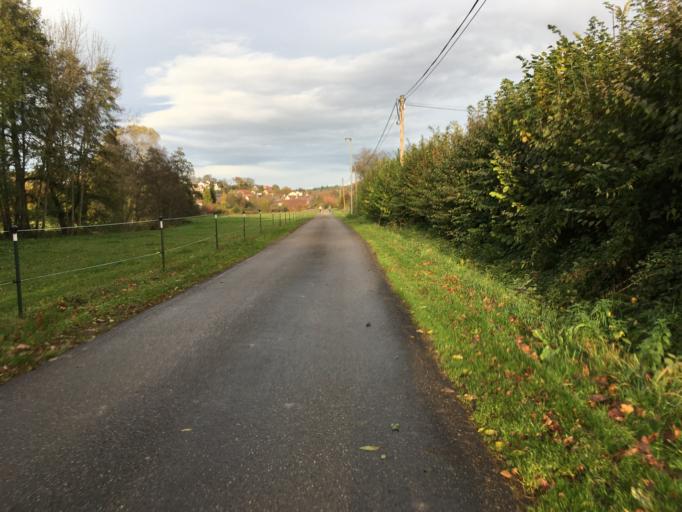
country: DE
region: Baden-Wuerttemberg
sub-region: Regierungsbezirk Stuttgart
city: Jagsthausen
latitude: 49.3611
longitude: 9.4799
